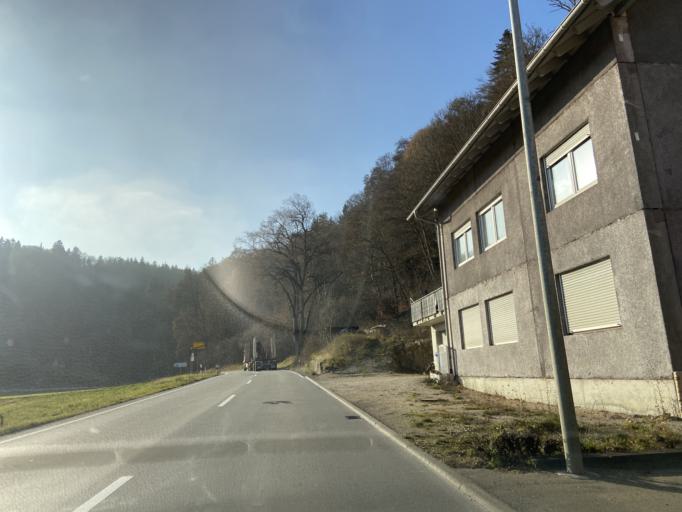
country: DE
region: Baden-Wuerttemberg
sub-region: Tuebingen Region
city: Veringenstadt
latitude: 48.1544
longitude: 9.1991
